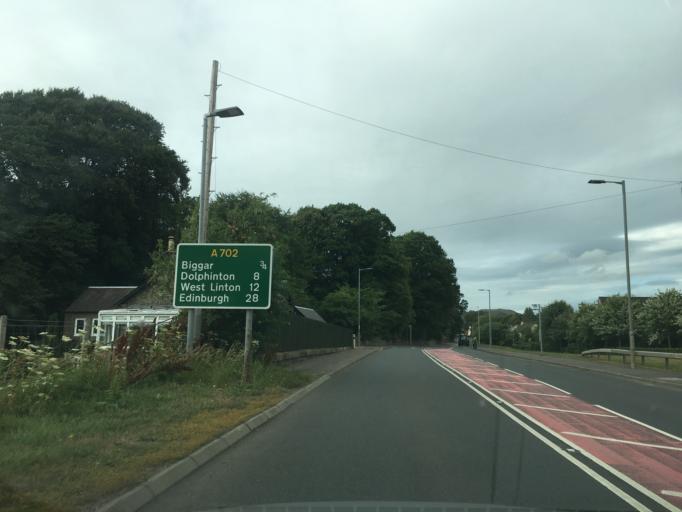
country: GB
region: Scotland
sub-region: South Lanarkshire
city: Biggar
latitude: 55.6160
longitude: -3.5377
